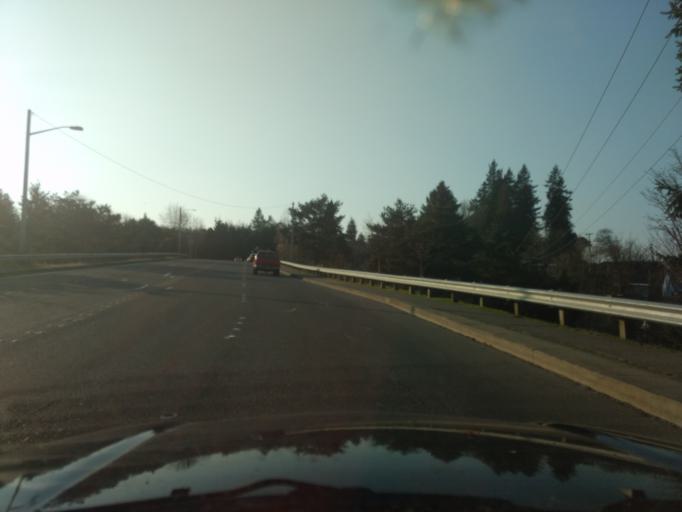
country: US
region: Washington
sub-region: Kitsap County
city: Navy Yard City
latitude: 47.5711
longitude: -122.6545
